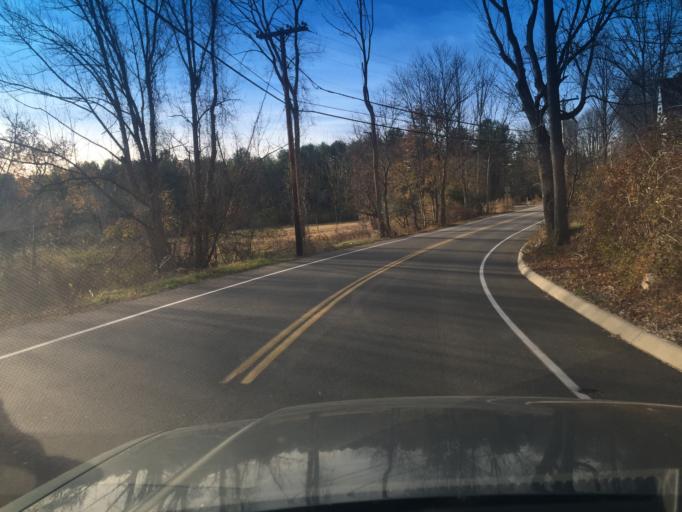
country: US
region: Maine
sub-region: York County
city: York Harbor
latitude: 43.1549
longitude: -70.6899
